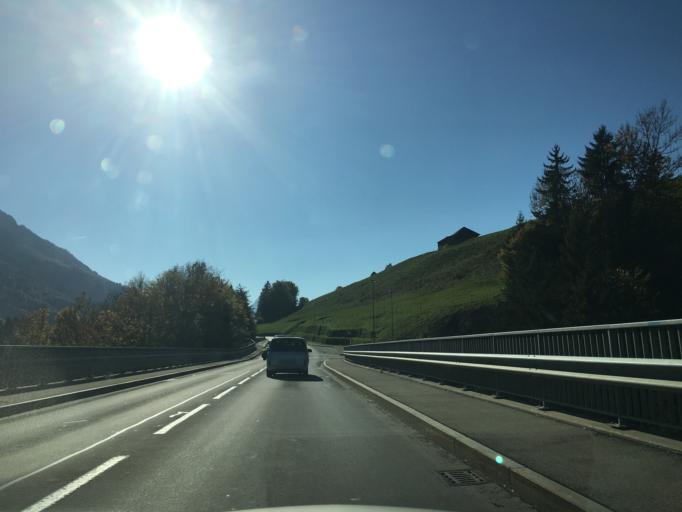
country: CH
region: Fribourg
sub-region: Gruyere District
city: Charmey
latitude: 46.6217
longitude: 7.1498
